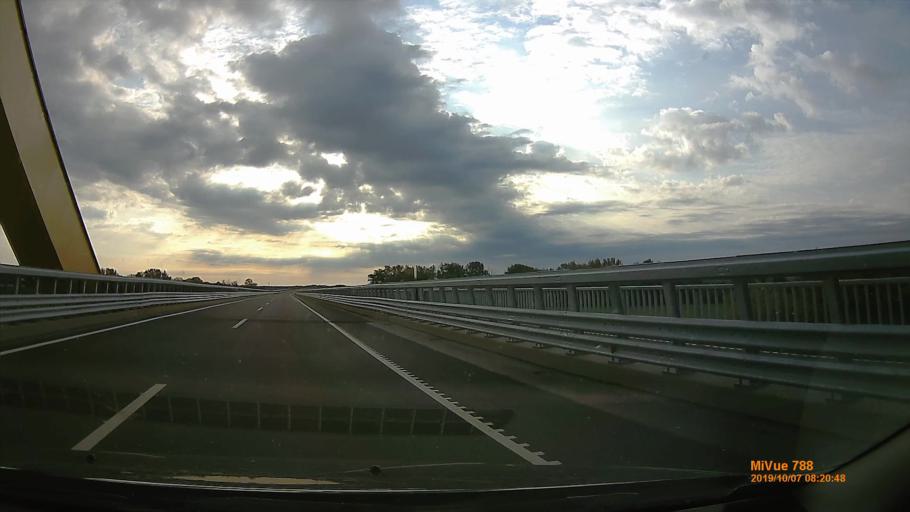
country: HU
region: Jasz-Nagykun-Szolnok
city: Kunszentmarton
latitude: 46.8649
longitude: 20.2874
